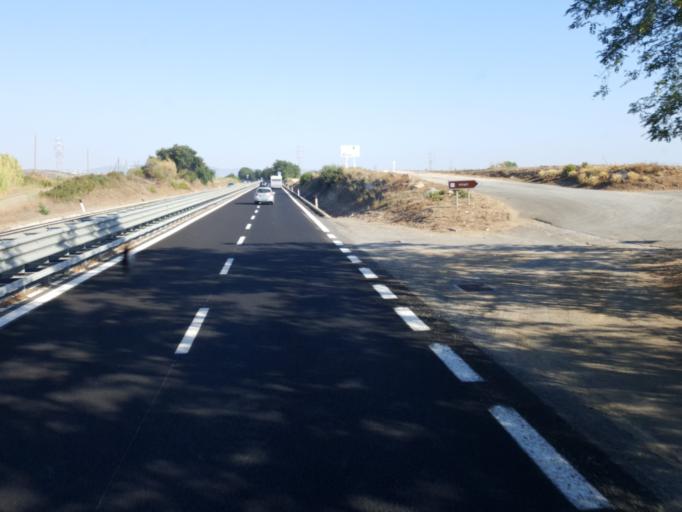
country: IT
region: Latium
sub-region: Provincia di Viterbo
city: Tarquinia
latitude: 42.2852
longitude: 11.6895
